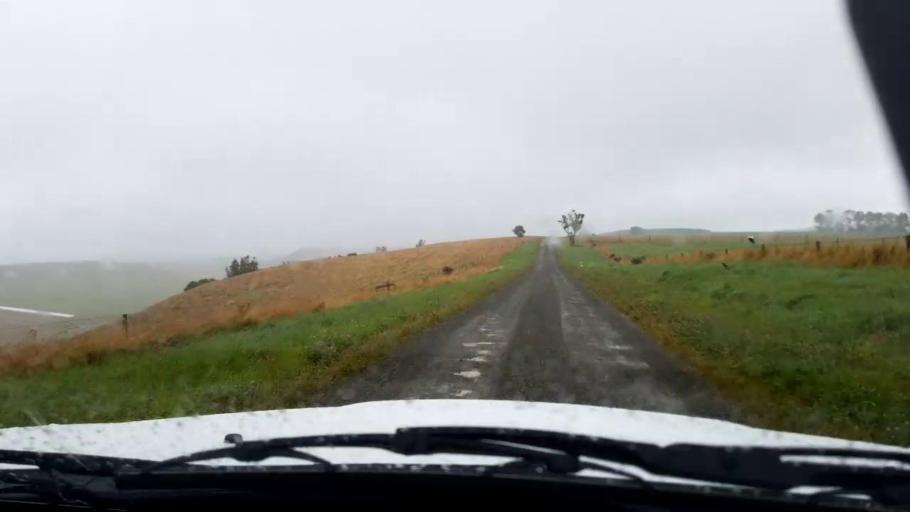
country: NZ
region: Canterbury
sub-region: Timaru District
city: Pleasant Point
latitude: -44.1689
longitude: 171.1645
